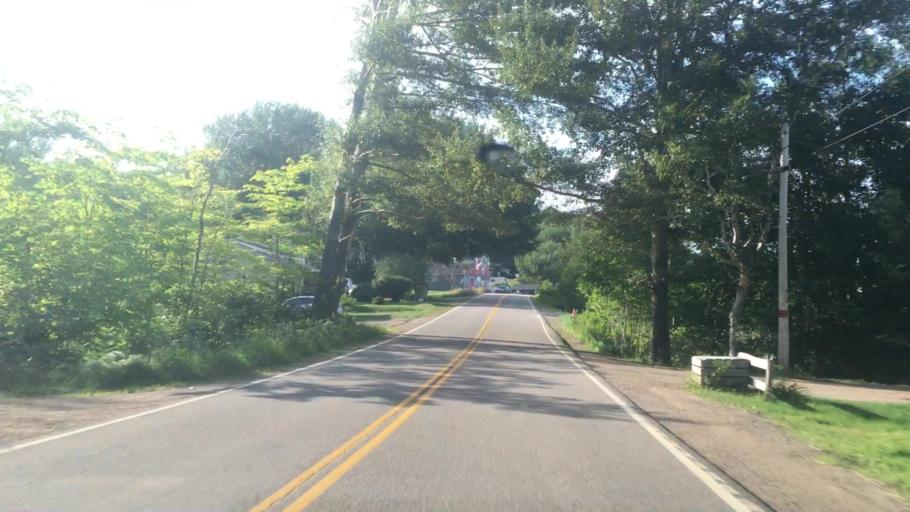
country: CA
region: Nova Scotia
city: Sydney Mines
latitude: 46.8215
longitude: -60.7978
